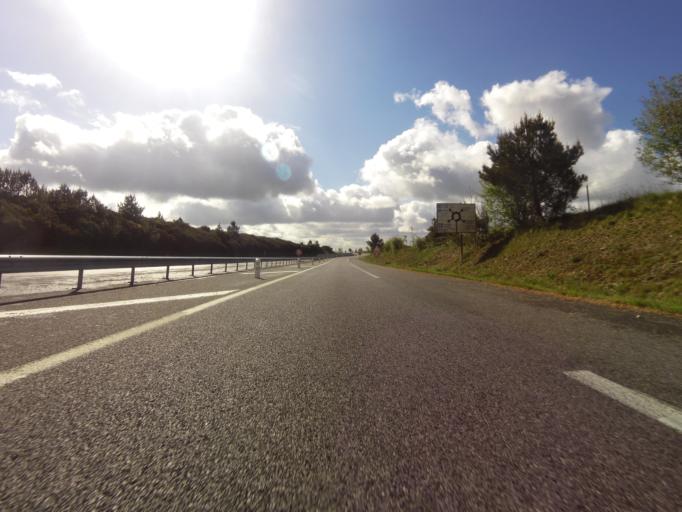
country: FR
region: Brittany
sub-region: Departement du Morbihan
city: Allaire
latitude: 47.6142
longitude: -2.1499
